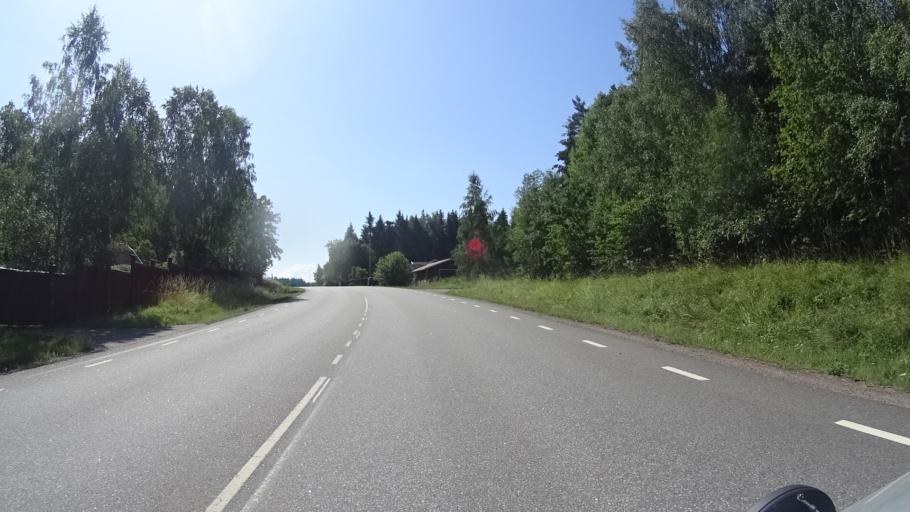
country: SE
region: OEstergoetland
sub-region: Vadstena Kommun
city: Herrestad
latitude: 58.2993
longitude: 14.9201
